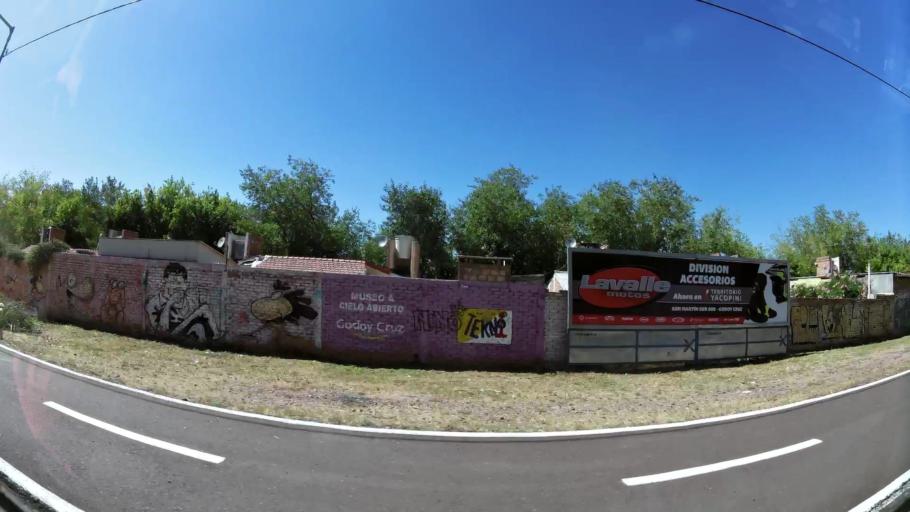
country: AR
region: Mendoza
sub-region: Departamento de Godoy Cruz
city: Godoy Cruz
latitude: -32.9527
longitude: -68.8556
